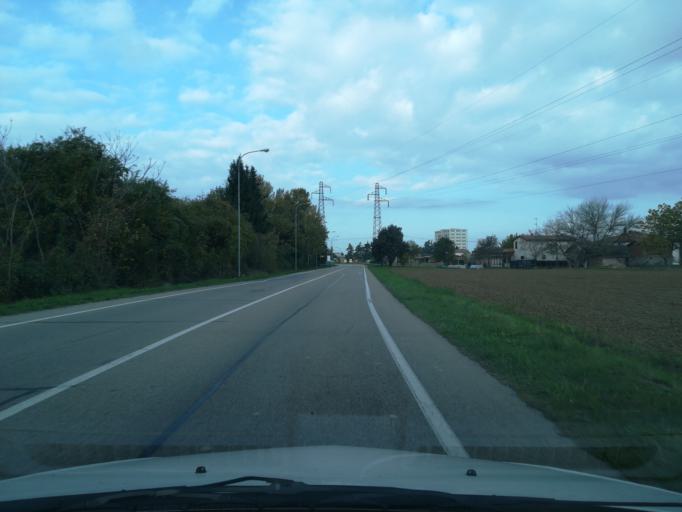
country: IT
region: Emilia-Romagna
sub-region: Provincia di Bologna
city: Imola
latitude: 44.3558
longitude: 11.7352
